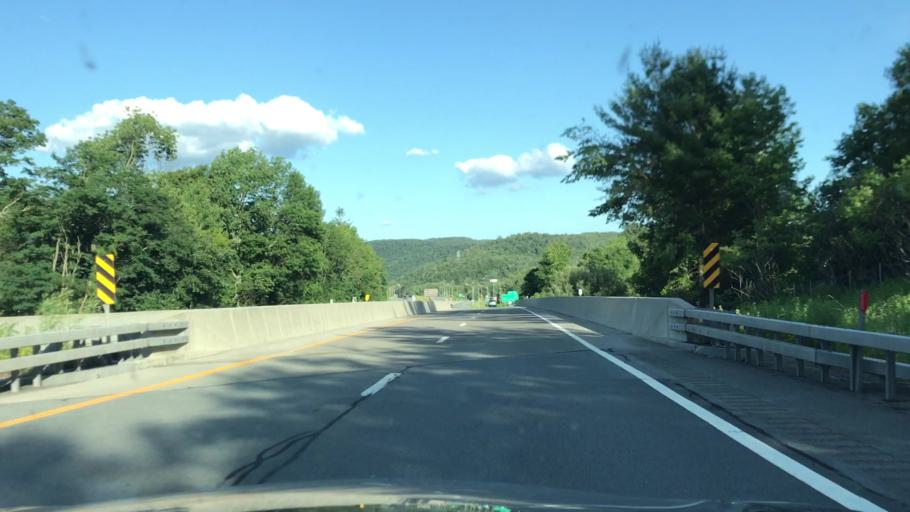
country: US
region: New York
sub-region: Sullivan County
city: Livingston Manor
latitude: 41.9343
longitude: -74.9209
